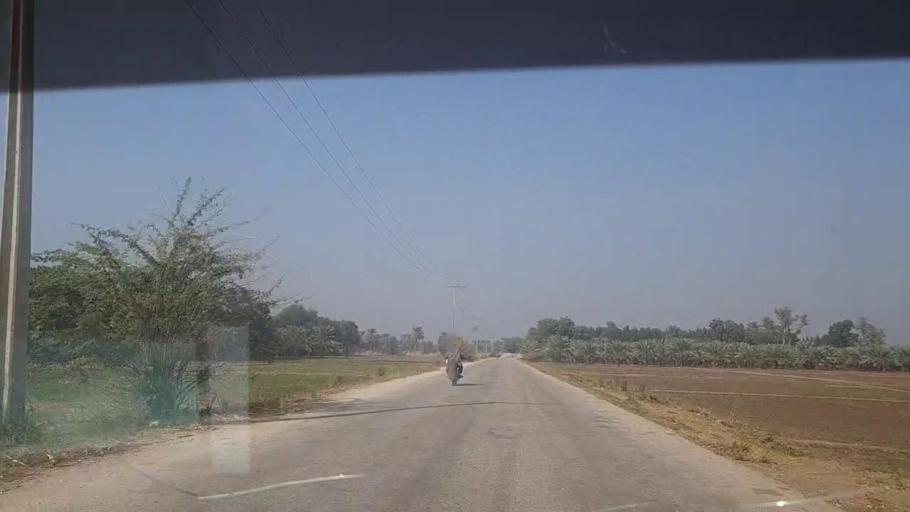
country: PK
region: Sindh
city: Kot Diji
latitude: 27.3684
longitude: 68.7015
